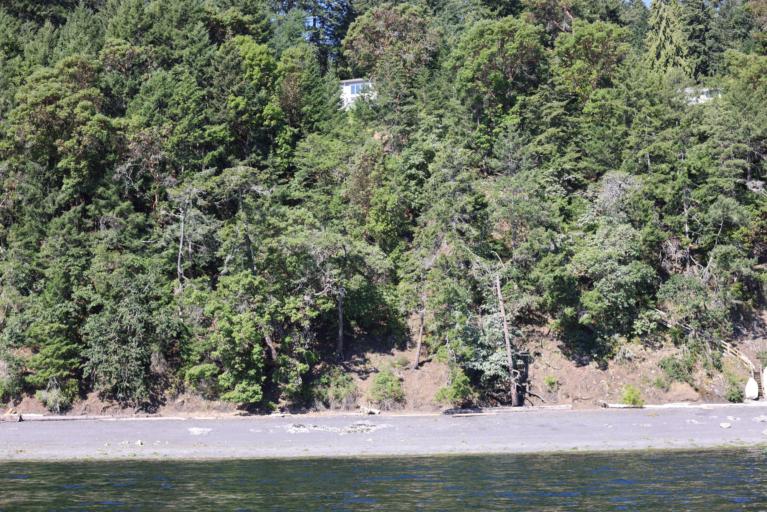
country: CA
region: British Columbia
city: North Cowichan
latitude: 48.8105
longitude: -123.6058
